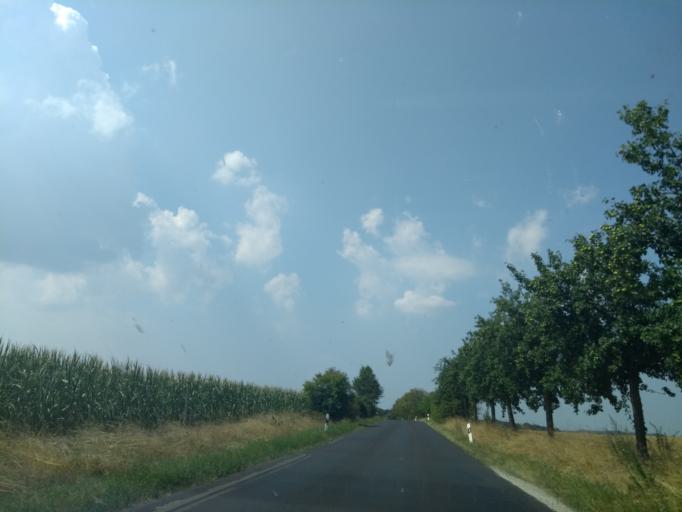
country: DE
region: Thuringia
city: Walpernhain
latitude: 50.9866
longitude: 11.9368
